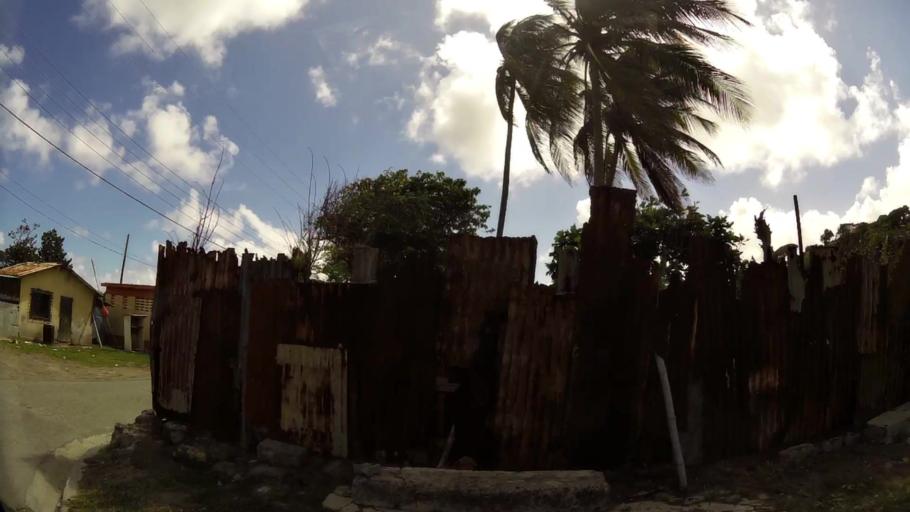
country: LC
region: Micoud Quarter
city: Micoud
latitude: 13.8196
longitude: -60.8953
